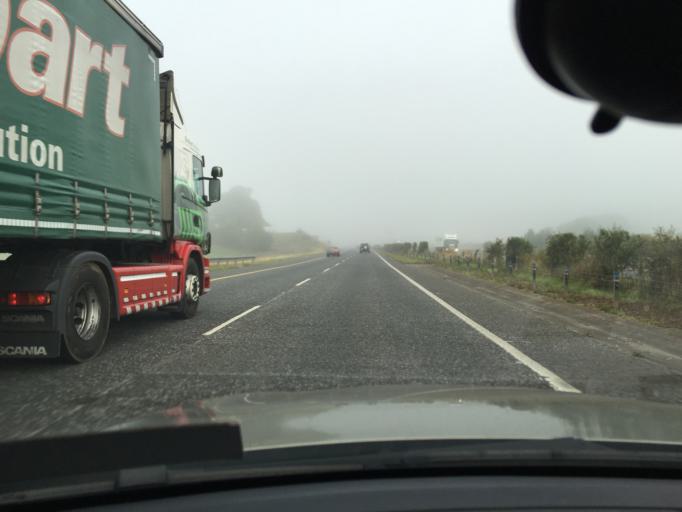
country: IE
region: Leinster
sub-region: An Mhi
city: Longwood
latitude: 53.4293
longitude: -6.9908
